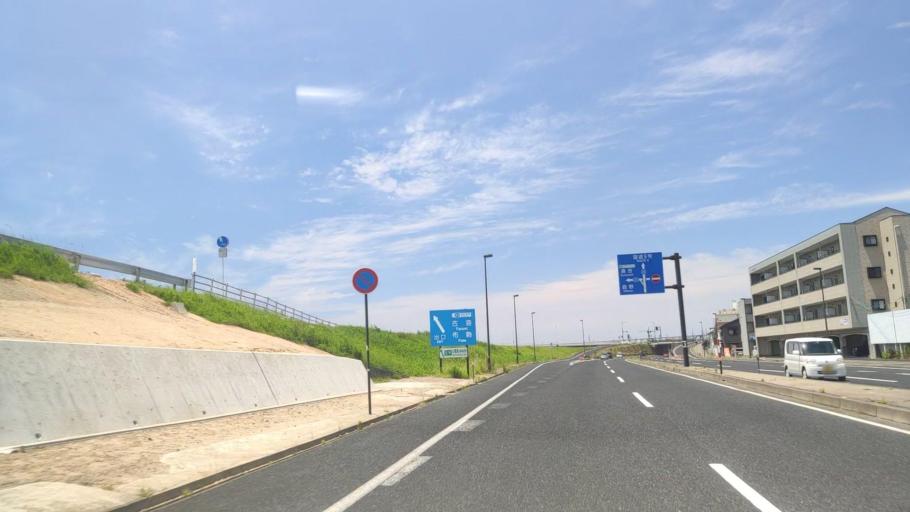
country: JP
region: Tottori
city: Tottori
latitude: 35.4935
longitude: 134.2190
